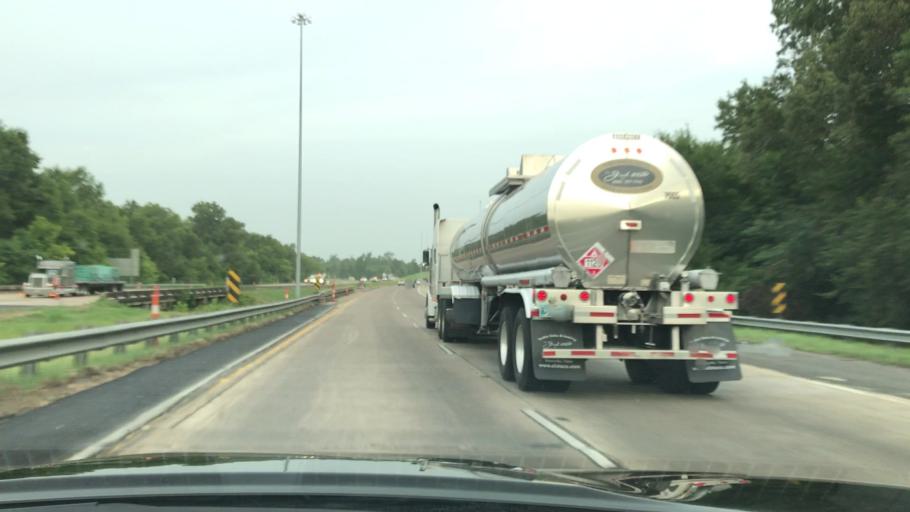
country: US
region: Louisiana
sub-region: Caddo Parish
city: Greenwood
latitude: 32.4519
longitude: -94.0166
